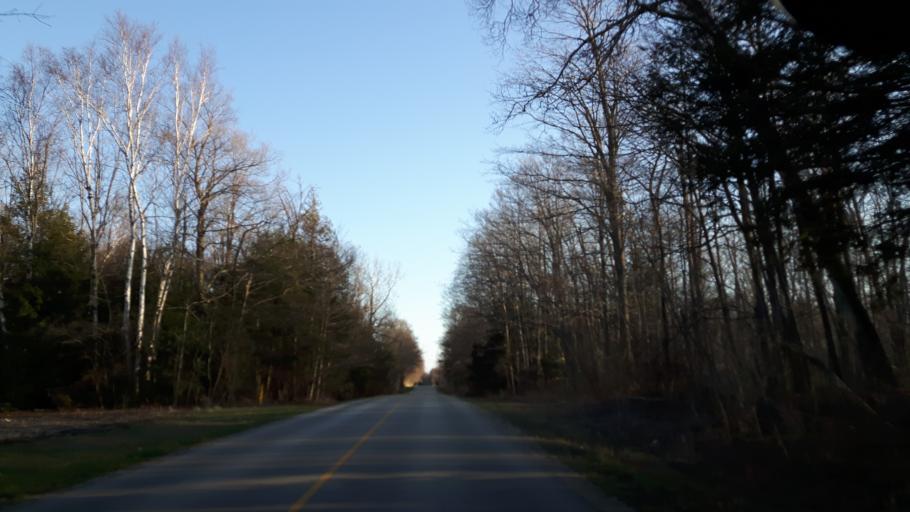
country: CA
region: Ontario
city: Goderich
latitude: 43.6195
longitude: -81.6847
